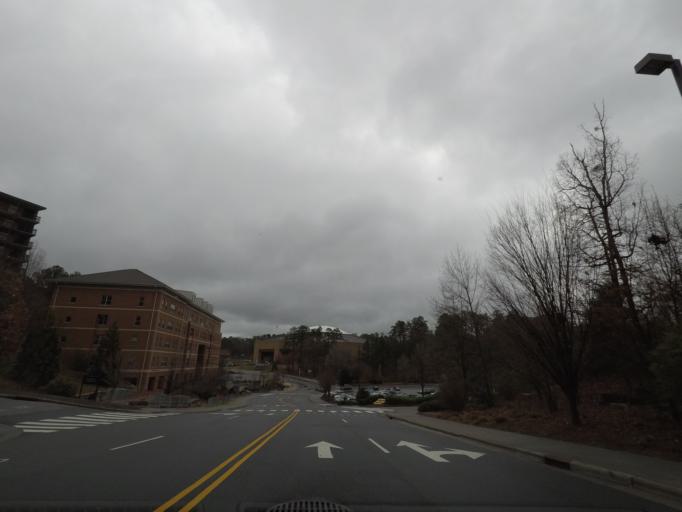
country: US
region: North Carolina
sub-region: Orange County
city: Chapel Hill
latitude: 35.9026
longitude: -79.0442
